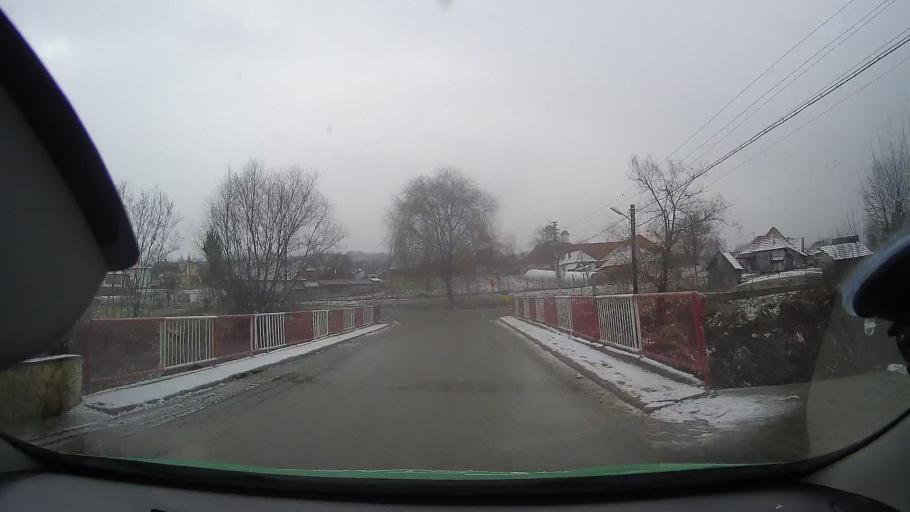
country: RO
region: Alba
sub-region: Comuna Farau
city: Farau
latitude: 46.3397
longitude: 24.0055
